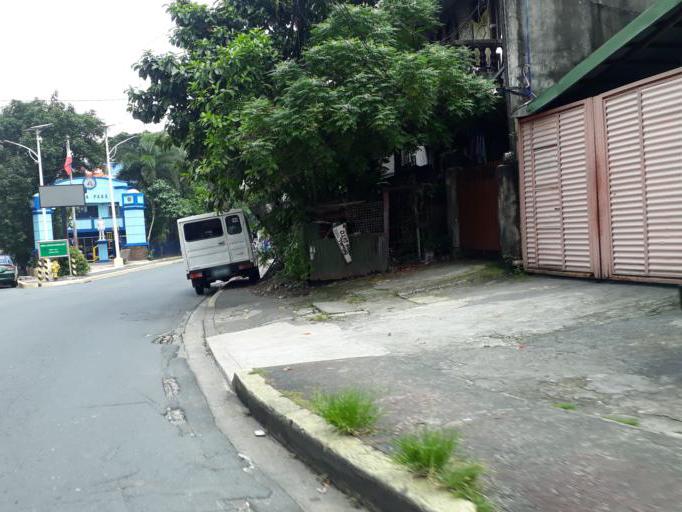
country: PH
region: Calabarzon
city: Bagong Pagasa
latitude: 14.6590
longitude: 121.0226
